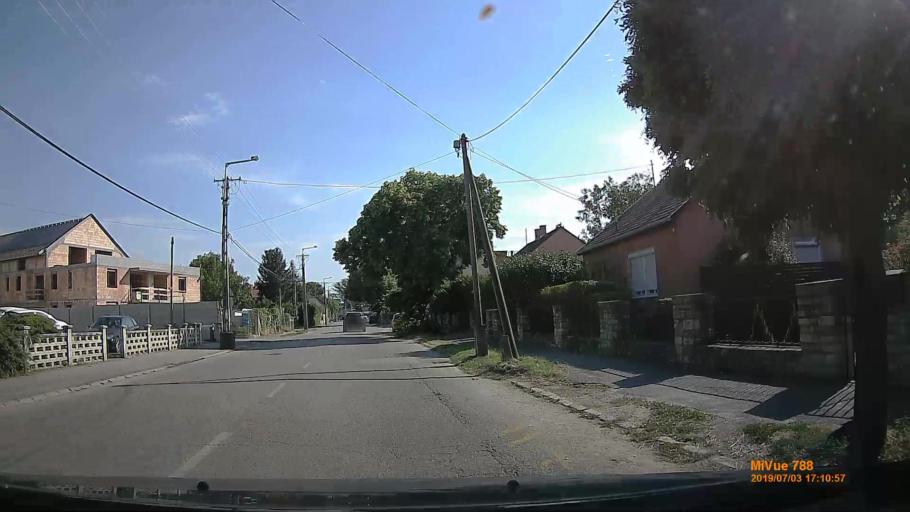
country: HU
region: Gyor-Moson-Sopron
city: Gyor
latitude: 47.7006
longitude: 17.6378
